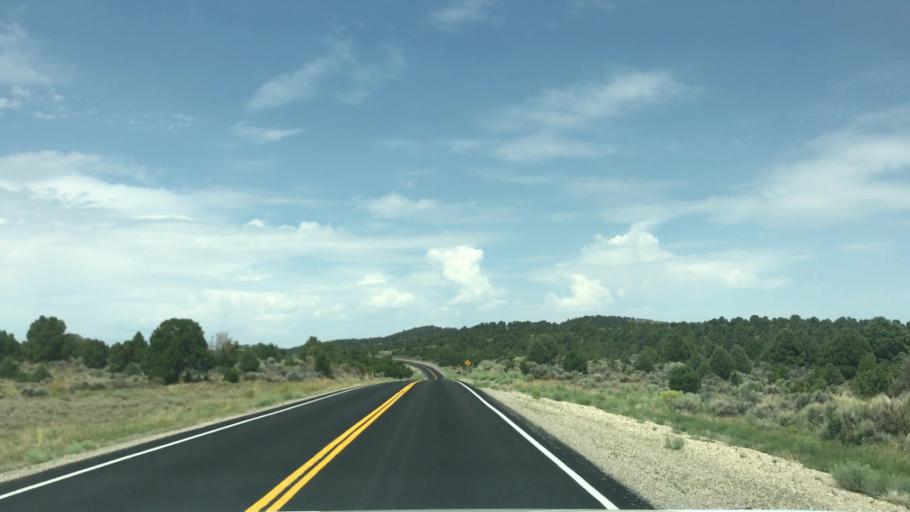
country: US
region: Nevada
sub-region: Eureka County
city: Eureka
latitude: 39.3939
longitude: -115.4598
